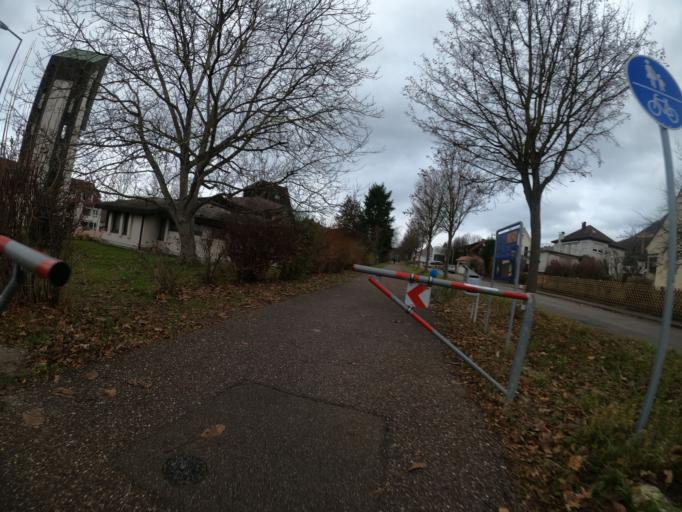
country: DE
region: Baden-Wuerttemberg
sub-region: Regierungsbezirk Stuttgart
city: Donzdorf
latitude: 48.6856
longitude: 9.8153
